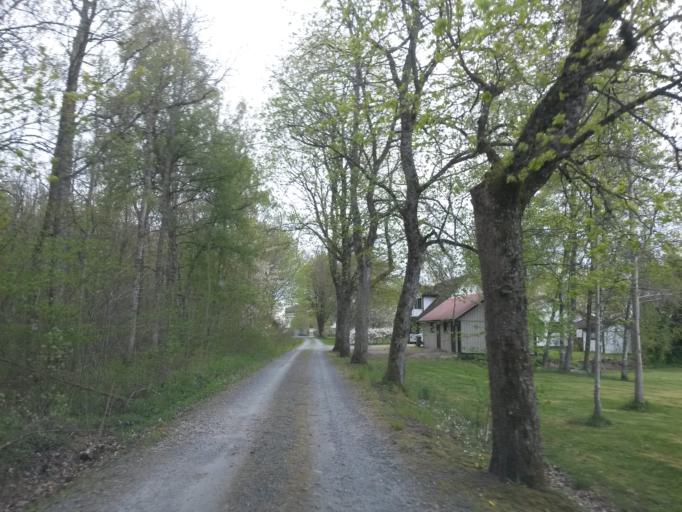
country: SE
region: Vaestra Goetaland
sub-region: Grastorps Kommun
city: Graestorp
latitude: 58.3959
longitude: 12.7961
